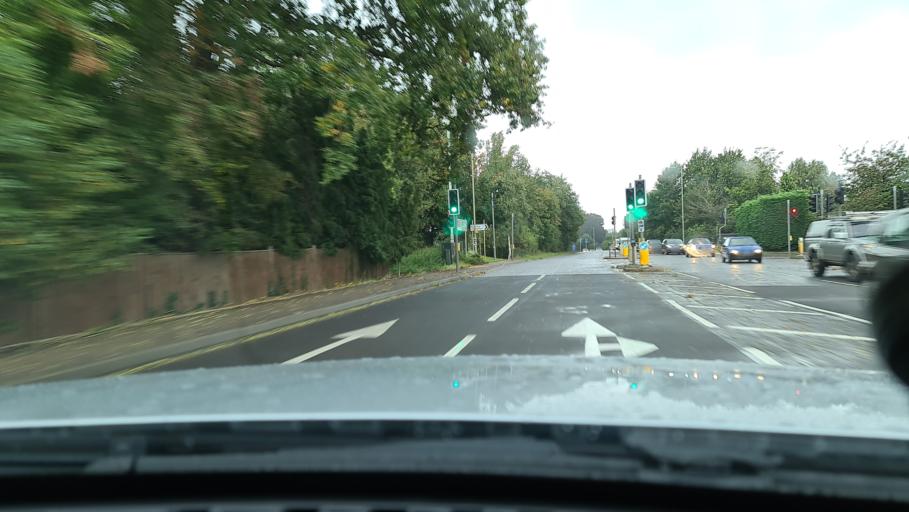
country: GB
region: England
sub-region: Oxfordshire
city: Adderbury
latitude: 52.0369
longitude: -1.3208
